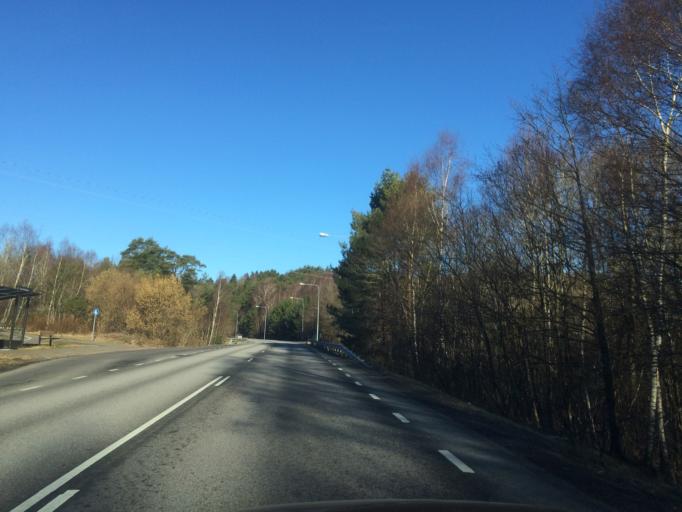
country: SE
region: Vaestra Goetaland
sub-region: Molndal
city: Kallered
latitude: 57.6282
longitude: 12.0314
